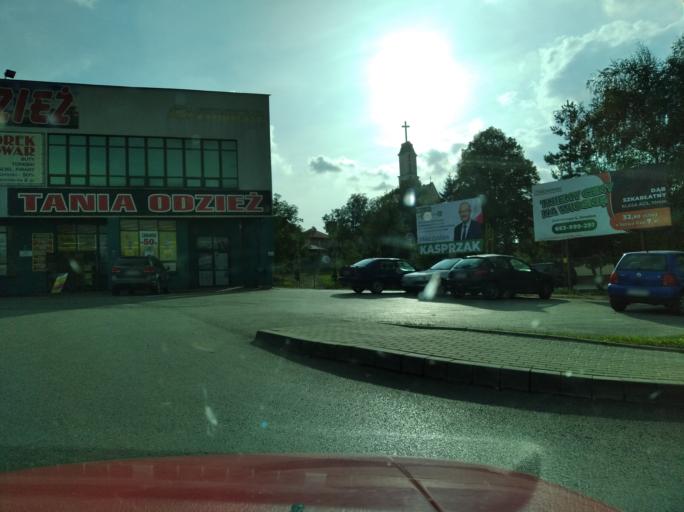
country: PL
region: Subcarpathian Voivodeship
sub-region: Powiat jaroslawski
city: Jaroslaw
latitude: 50.0093
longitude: 22.6753
